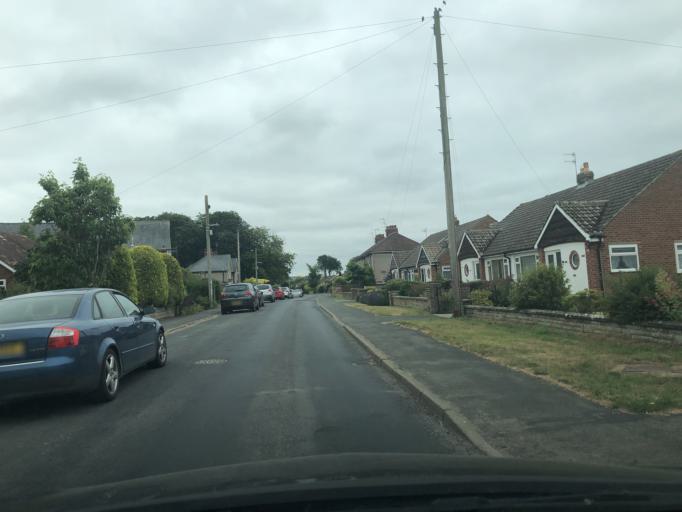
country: GB
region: England
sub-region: North Yorkshire
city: East Ayton
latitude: 54.2467
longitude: -0.4877
